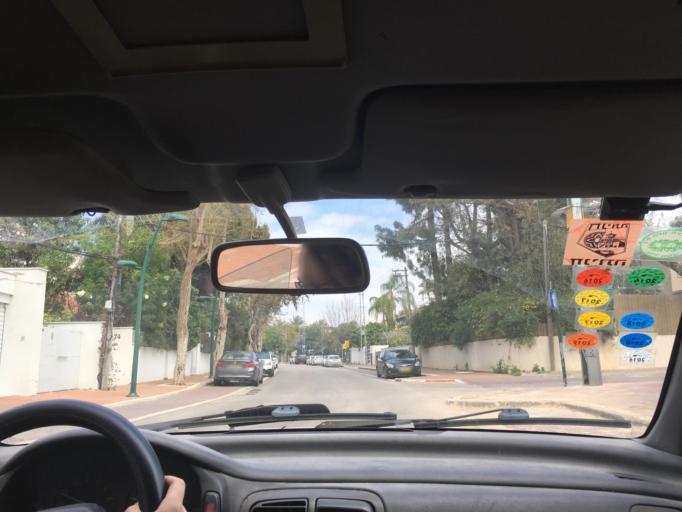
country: IL
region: Tel Aviv
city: Ramat HaSharon
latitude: 32.1453
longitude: 34.8323
